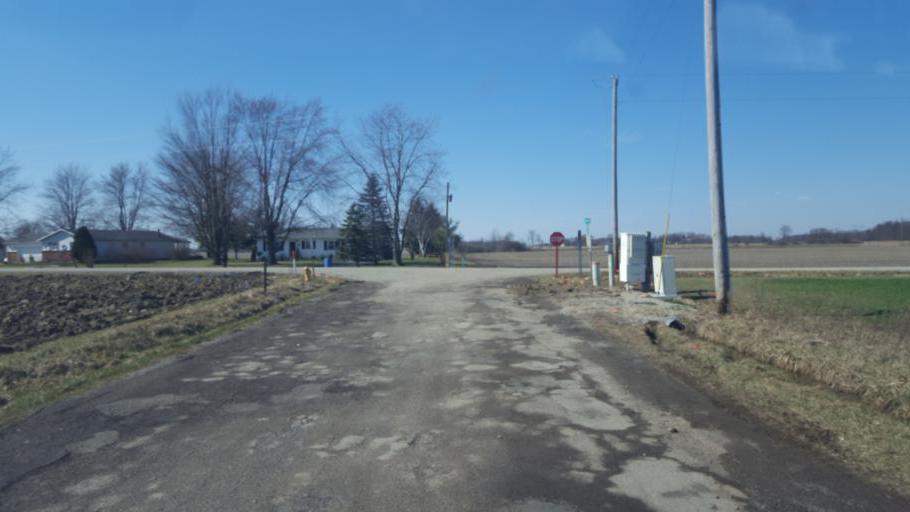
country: US
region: Ohio
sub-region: Morrow County
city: Cardington
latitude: 40.4903
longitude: -82.9627
